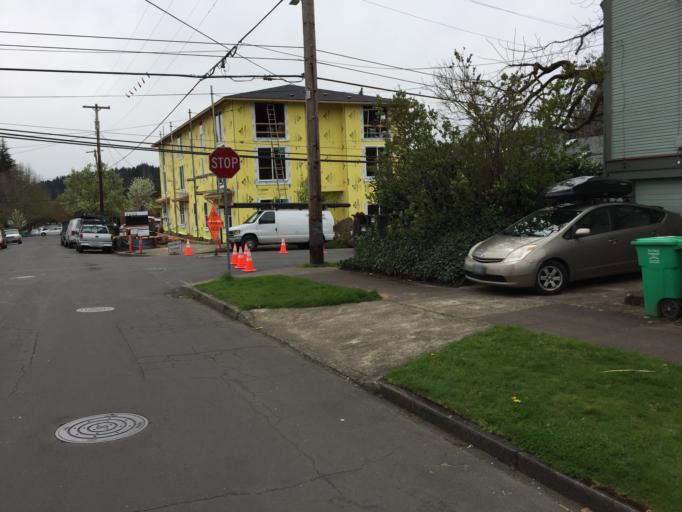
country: US
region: Oregon
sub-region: Clackamas County
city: Milwaukie
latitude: 45.4653
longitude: -122.6591
